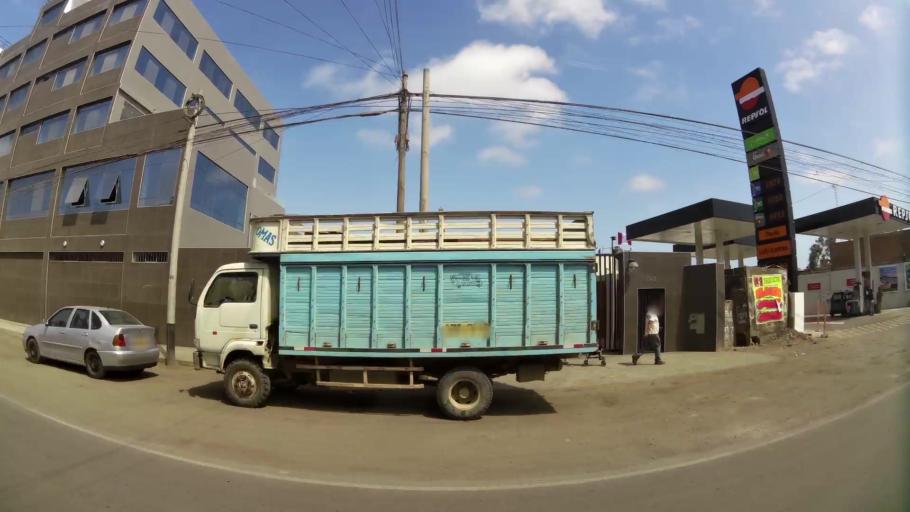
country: PE
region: Lima
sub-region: Provincia de Canete
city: Mala
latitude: -12.6582
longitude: -76.6350
